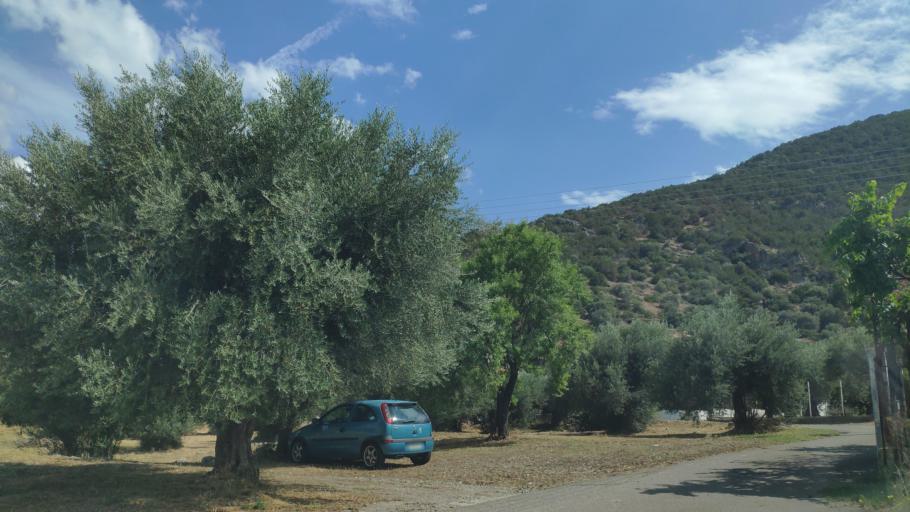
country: GR
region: West Greece
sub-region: Nomos Achaias
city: Aigio
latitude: 38.3697
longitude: 22.1261
